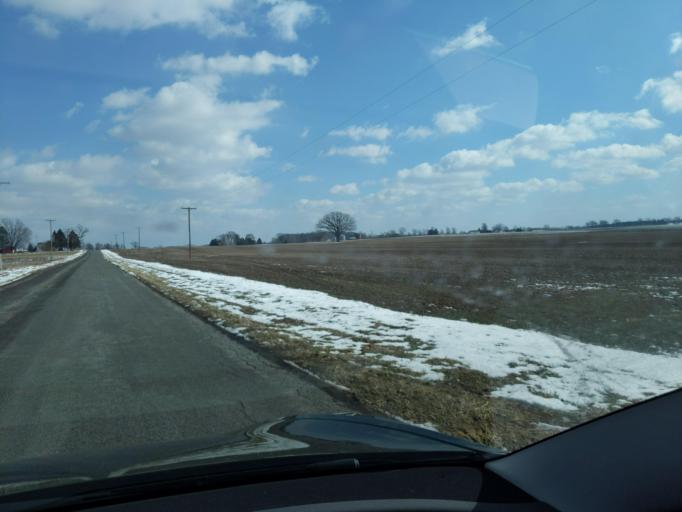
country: US
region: Michigan
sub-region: Ingham County
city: Webberville
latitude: 42.6147
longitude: -84.1802
